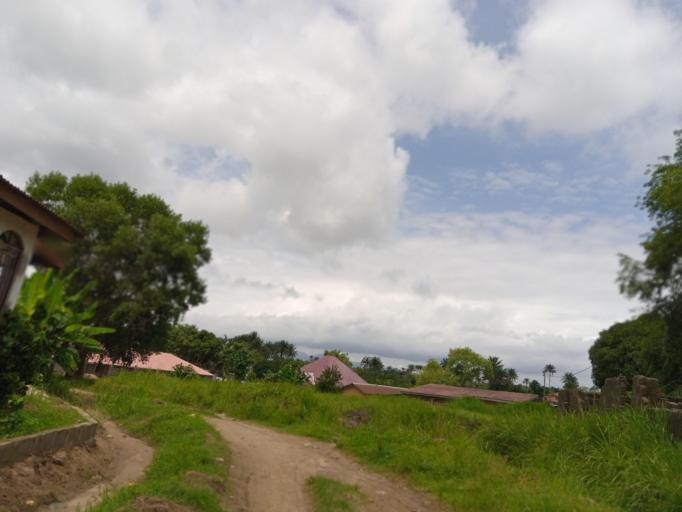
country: SL
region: Northern Province
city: Masoyila
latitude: 8.5929
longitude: -13.1837
